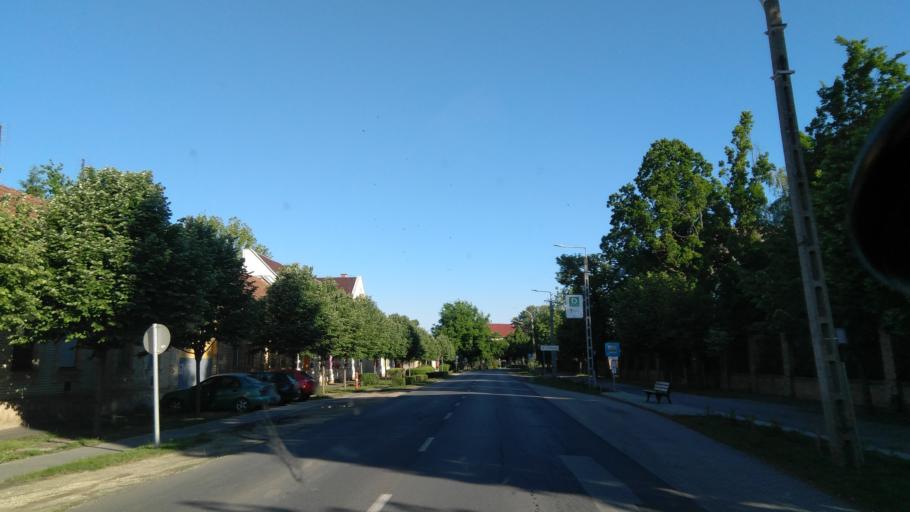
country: HU
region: Bekes
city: Gyula
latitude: 46.6394
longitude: 21.2759
